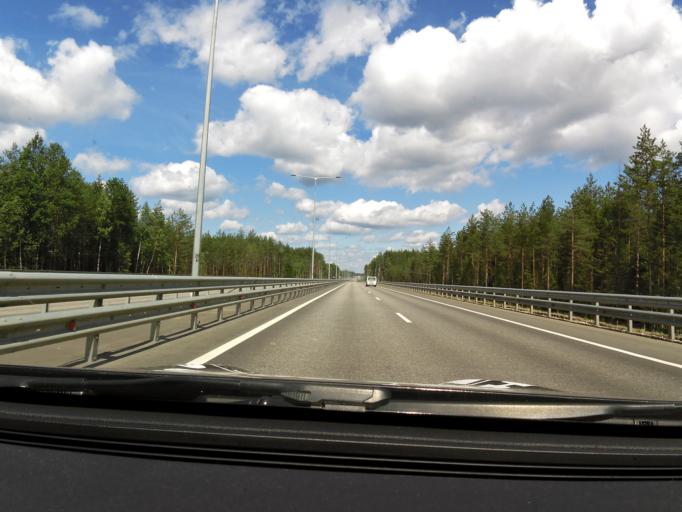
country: RU
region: Tverskaya
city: Krasnomayskiy
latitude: 57.5748
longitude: 34.2595
